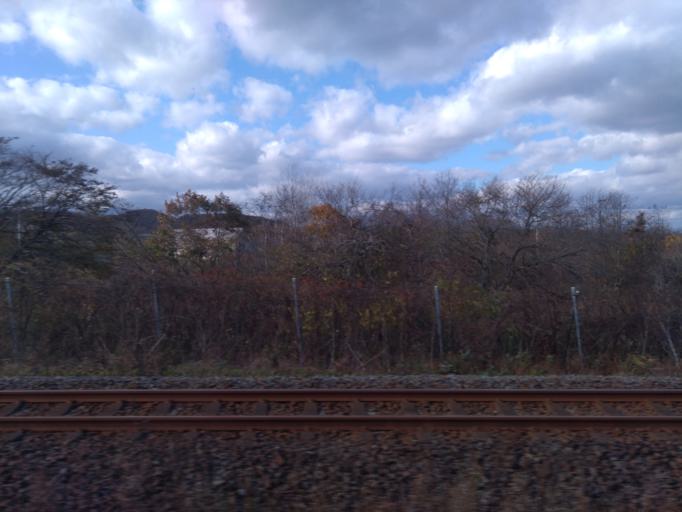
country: JP
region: Hokkaido
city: Shiraoi
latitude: 42.4987
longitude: 141.2695
